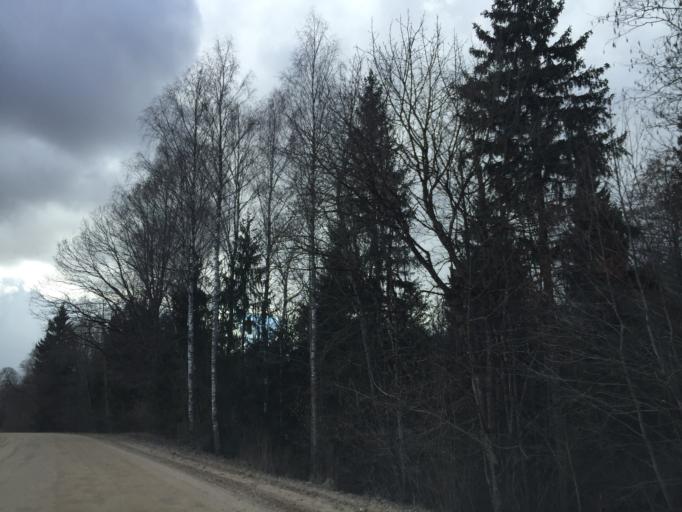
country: LV
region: Akniste
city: Akniste
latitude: 56.1079
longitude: 25.8282
